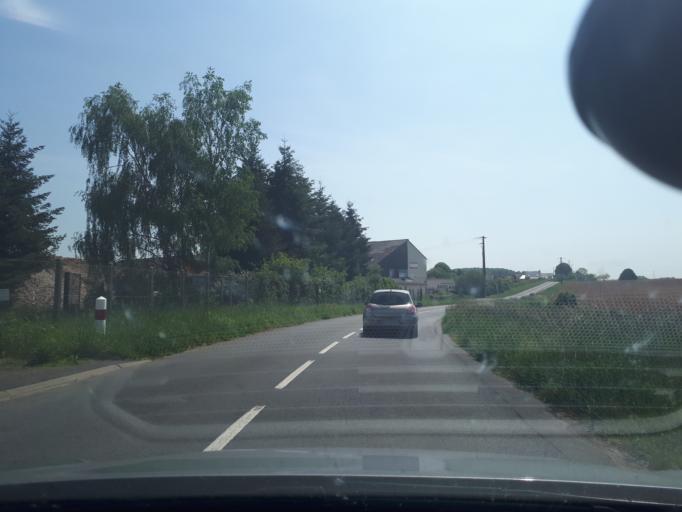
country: FR
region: Pays de la Loire
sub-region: Departement de la Sarthe
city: Le Breil-sur-Merize
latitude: 48.0179
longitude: 0.4643
